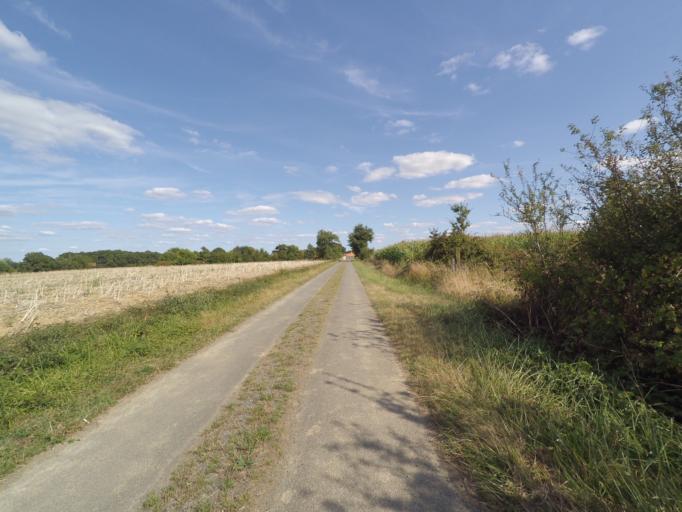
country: FR
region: Pays de la Loire
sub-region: Departement de la Loire-Atlantique
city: Vieillevigne
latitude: 46.9553
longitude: -1.4405
